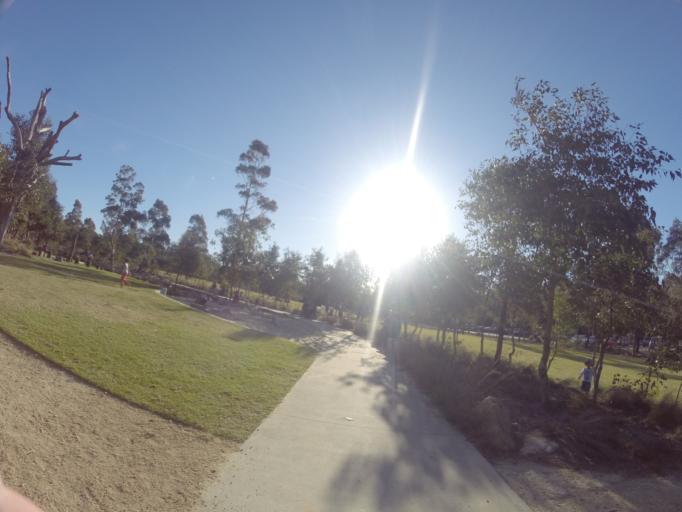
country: AU
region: New South Wales
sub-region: Fairfield
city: Horsley Park
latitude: -33.8507
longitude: 150.8709
